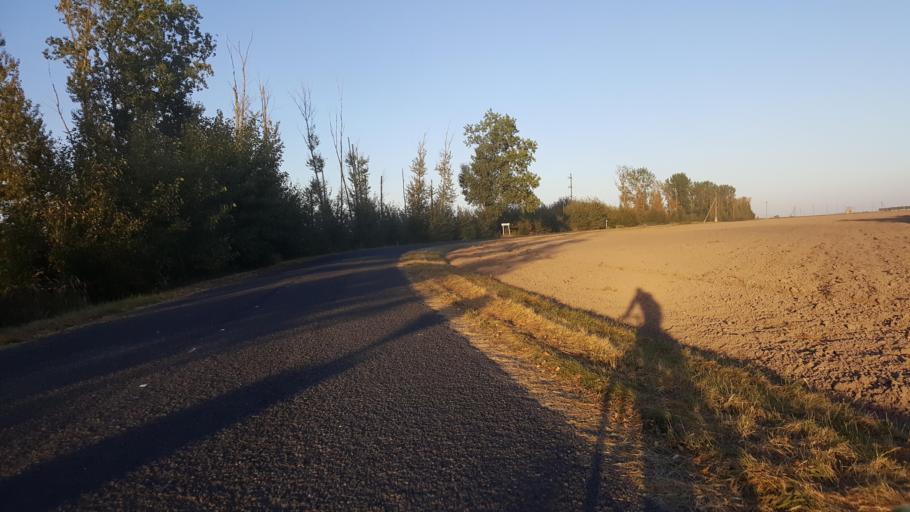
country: BY
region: Brest
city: Vysokaye
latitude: 52.2967
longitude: 23.5224
